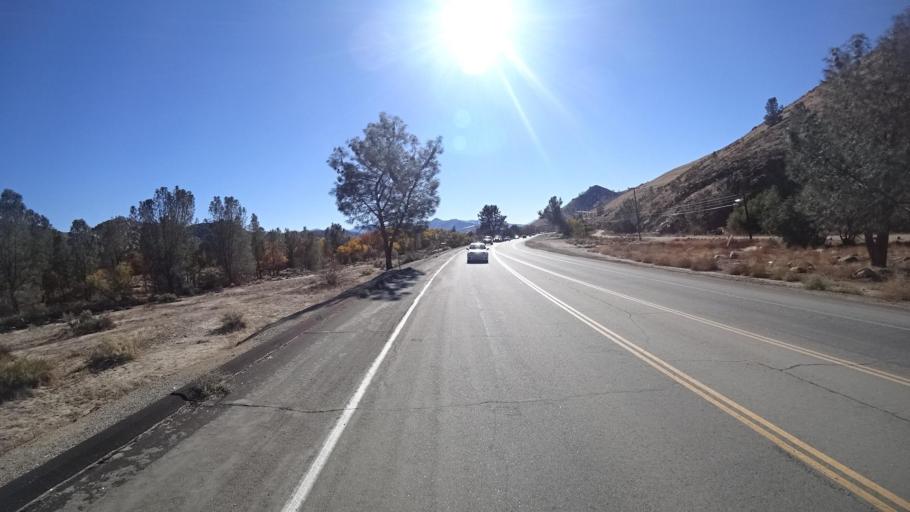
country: US
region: California
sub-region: Kern County
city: Kernville
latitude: 35.7470
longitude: -118.4220
